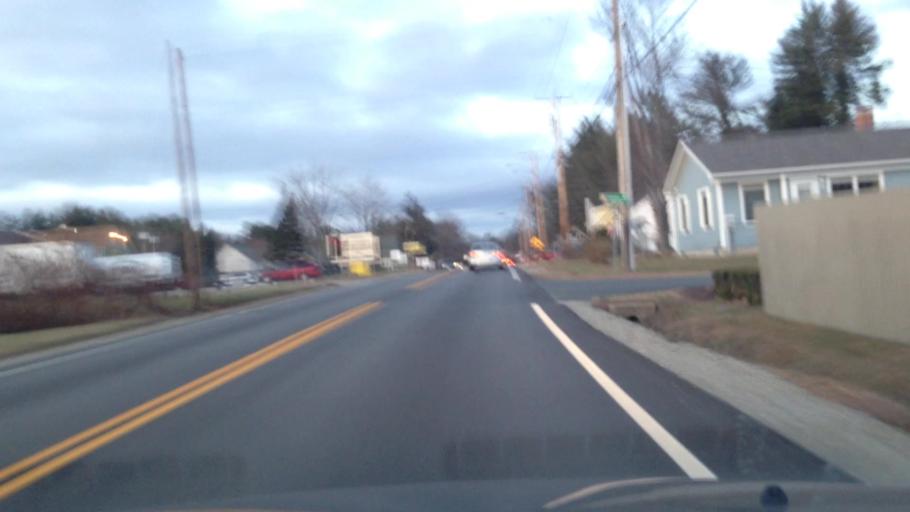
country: US
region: New Hampshire
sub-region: Cheshire County
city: Keene
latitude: 42.9022
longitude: -72.2653
